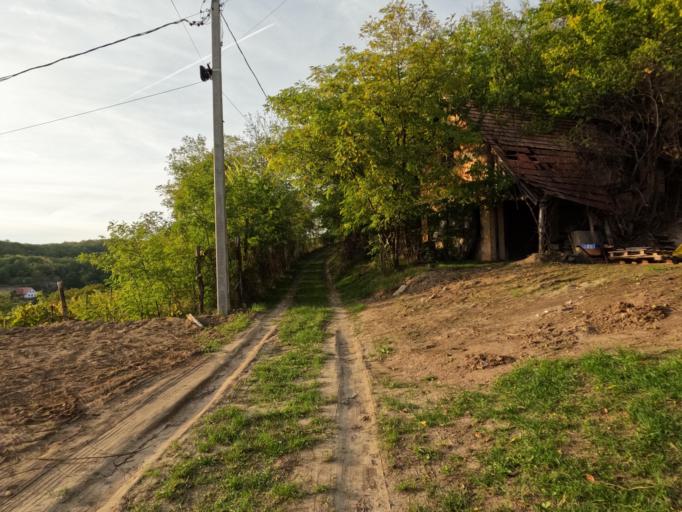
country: HU
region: Tolna
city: Szekszard
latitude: 46.3380
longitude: 18.6729
